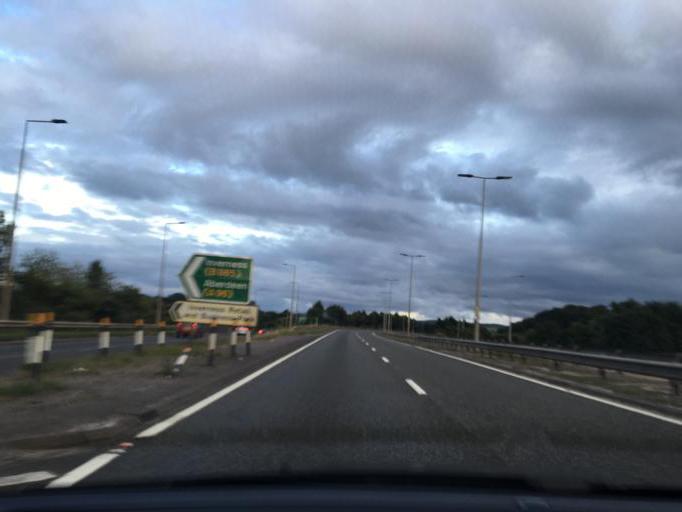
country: GB
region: Scotland
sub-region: Highland
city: Inverness
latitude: 57.4837
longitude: -4.1972
